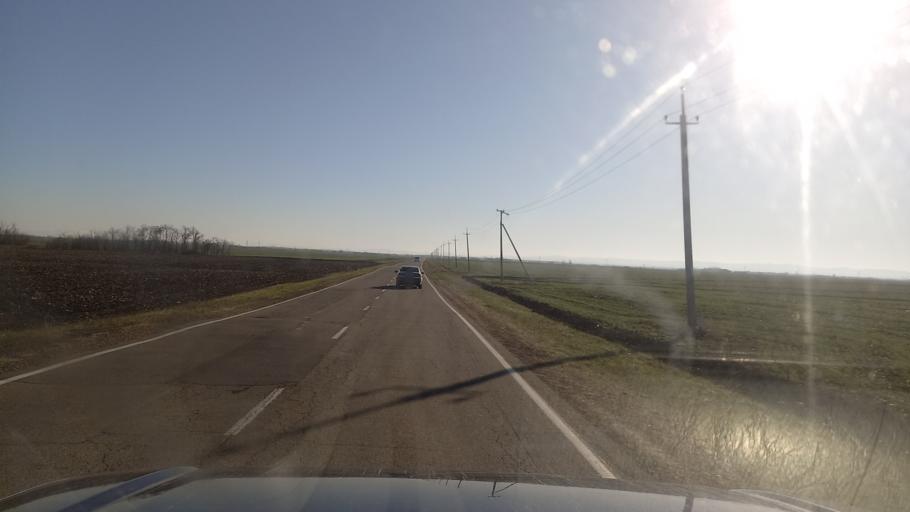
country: RU
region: Adygeya
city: Takhtamukay
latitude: 44.9031
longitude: 39.0520
